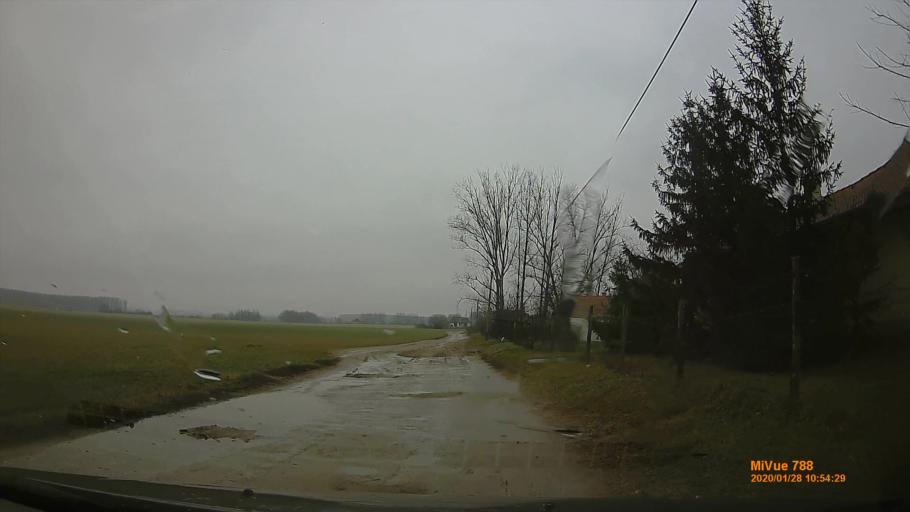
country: HU
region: Pest
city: Monor
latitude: 47.3662
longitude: 19.4270
